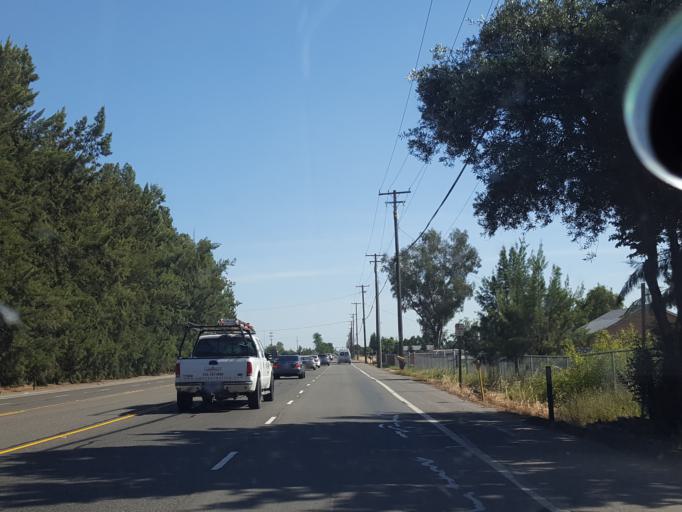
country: US
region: California
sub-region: Sacramento County
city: Vineyard
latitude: 38.5033
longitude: -121.3351
